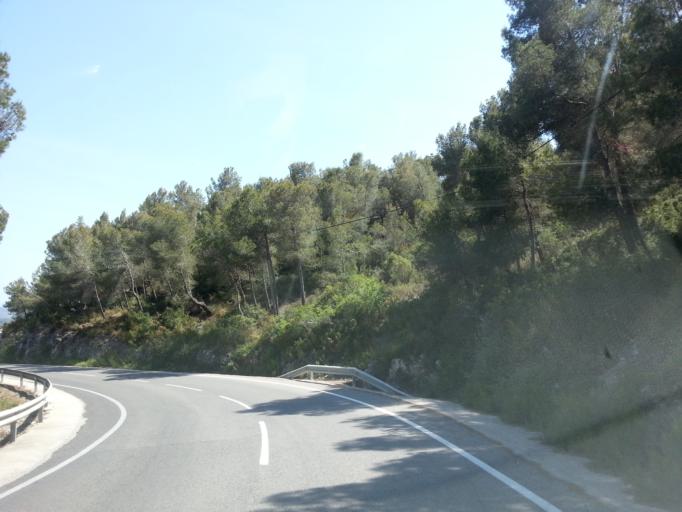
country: ES
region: Catalonia
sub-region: Provincia de Tarragona
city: Alcover
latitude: 41.2713
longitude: 1.1715
